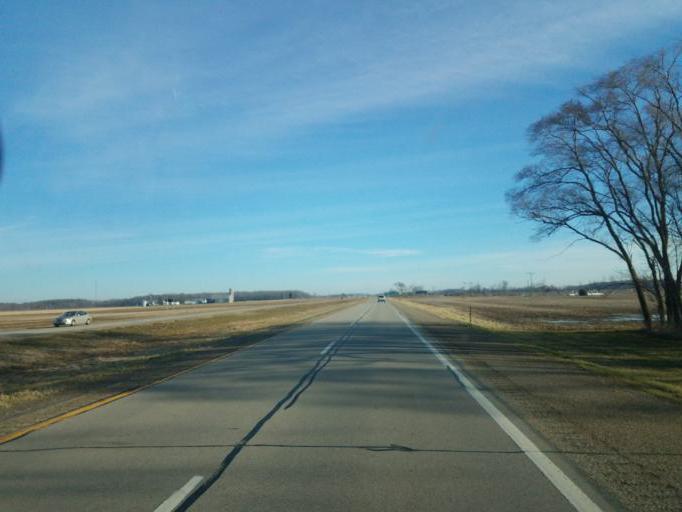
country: US
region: Michigan
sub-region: Gratiot County
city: Ithaca
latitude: 43.1551
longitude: -84.5632
